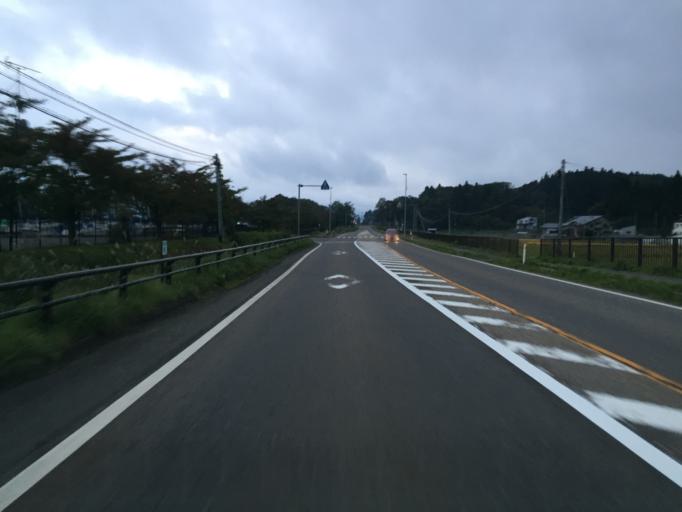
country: JP
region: Fukushima
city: Inawashiro
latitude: 37.5305
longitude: 140.0569
